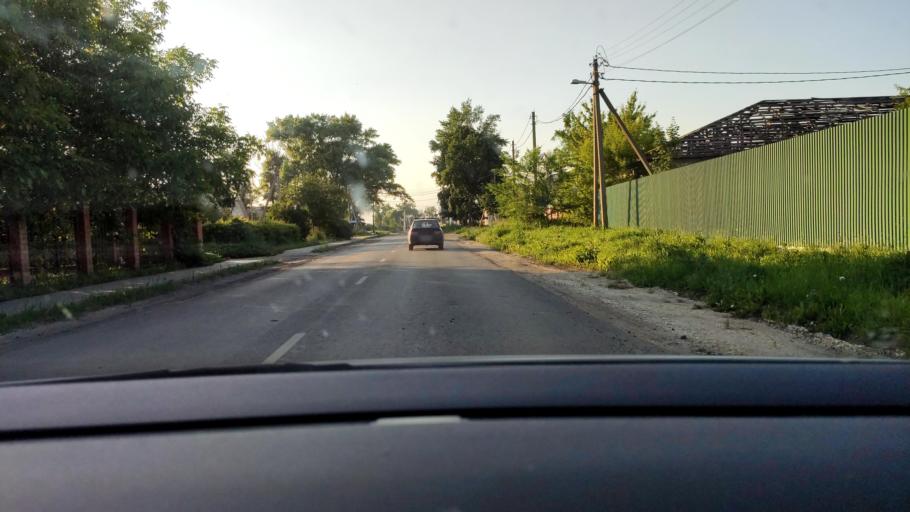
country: RU
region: Voronezj
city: Maslovka
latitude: 51.5386
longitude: 39.3419
